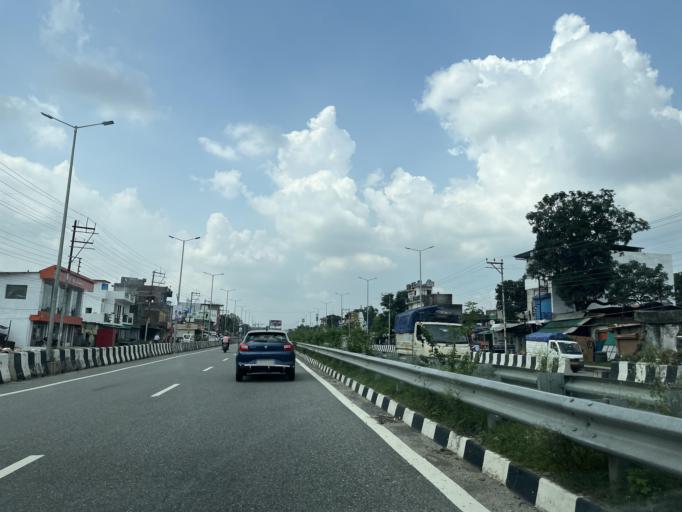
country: IN
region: Uttarakhand
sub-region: Dehradun
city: Raipur
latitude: 30.2577
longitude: 78.0907
